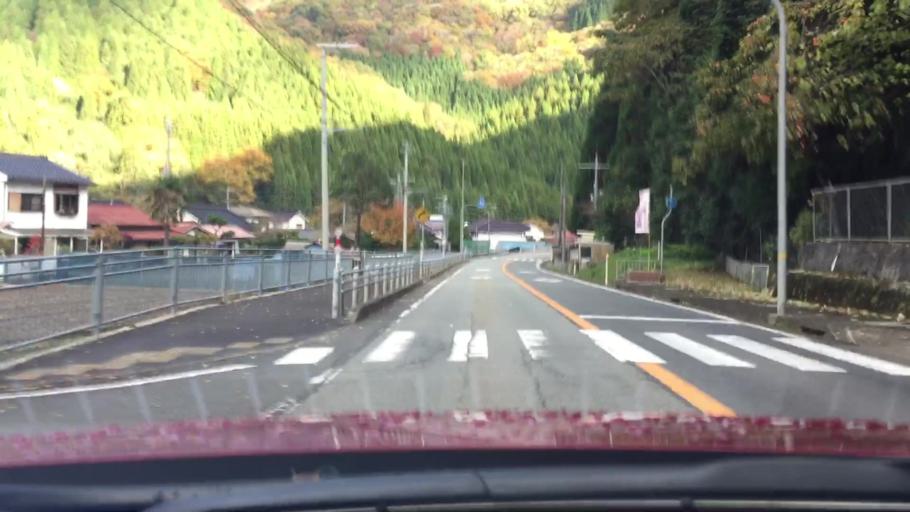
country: JP
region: Hyogo
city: Yamazakicho-nakabirose
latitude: 35.1865
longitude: 134.5311
